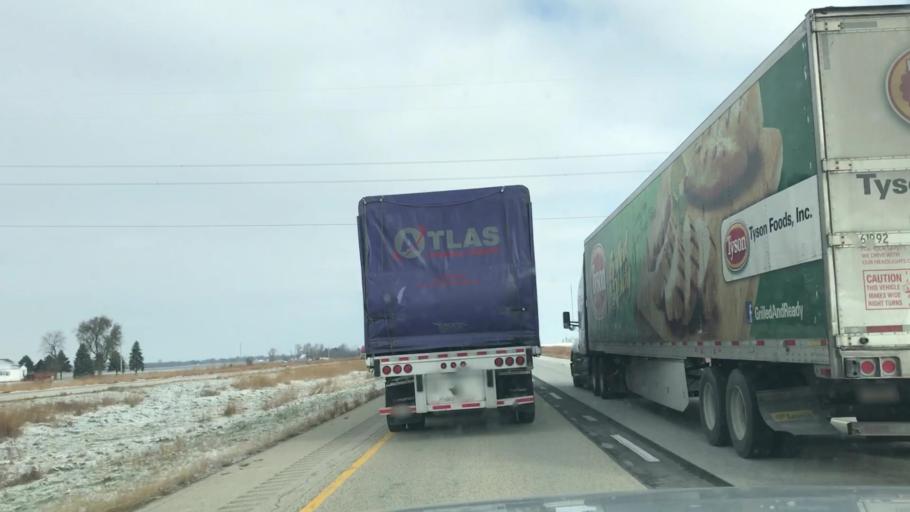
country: US
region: Illinois
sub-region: Sangamon County
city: Divernon
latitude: 39.5302
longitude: -89.6456
